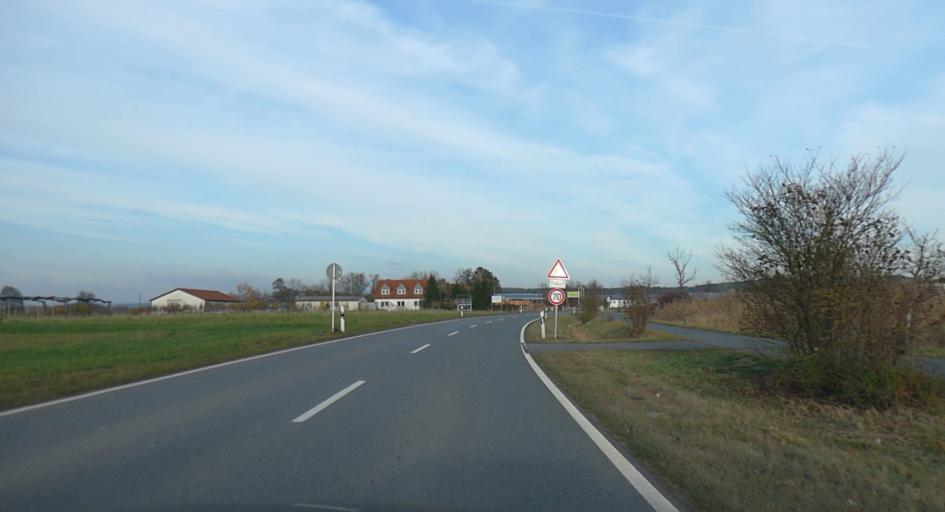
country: DE
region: Bavaria
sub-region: Upper Franconia
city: Poxdorf
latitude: 49.6625
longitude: 11.0612
